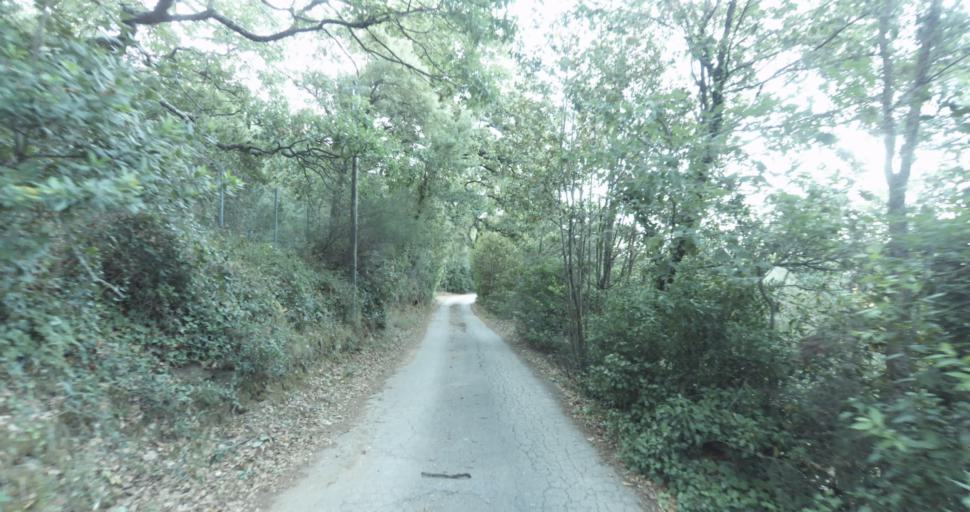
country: FR
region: Provence-Alpes-Cote d'Azur
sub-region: Departement du Var
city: Gassin
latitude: 43.2236
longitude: 6.5908
